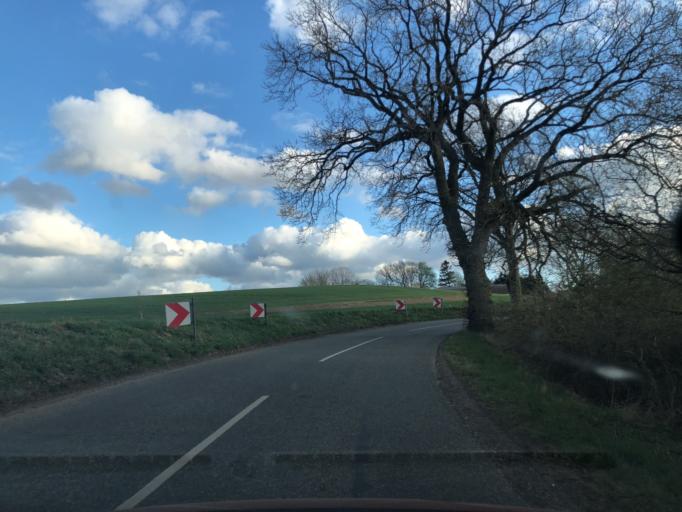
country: DK
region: Zealand
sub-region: Lejre Kommune
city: Kirke Hvalso
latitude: 55.5091
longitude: 11.8691
